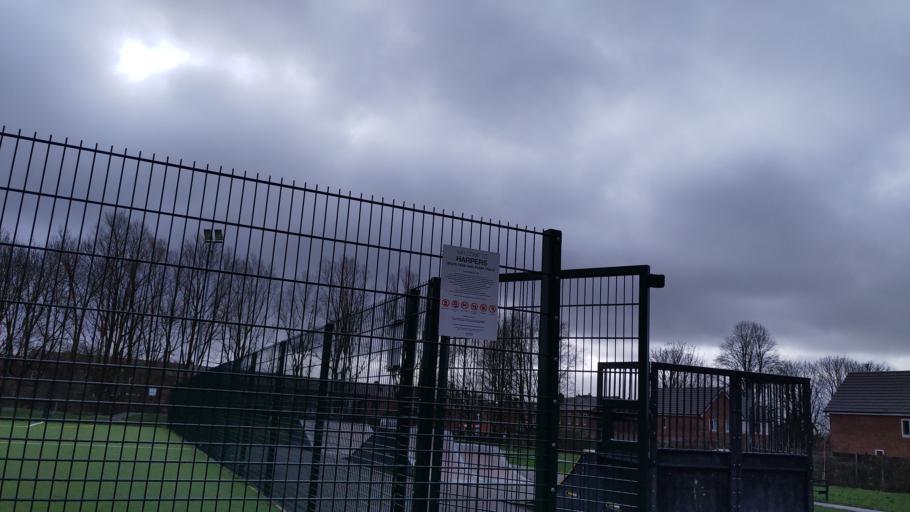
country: GB
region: England
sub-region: Lancashire
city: Chorley
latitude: 53.6603
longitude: -2.6223
